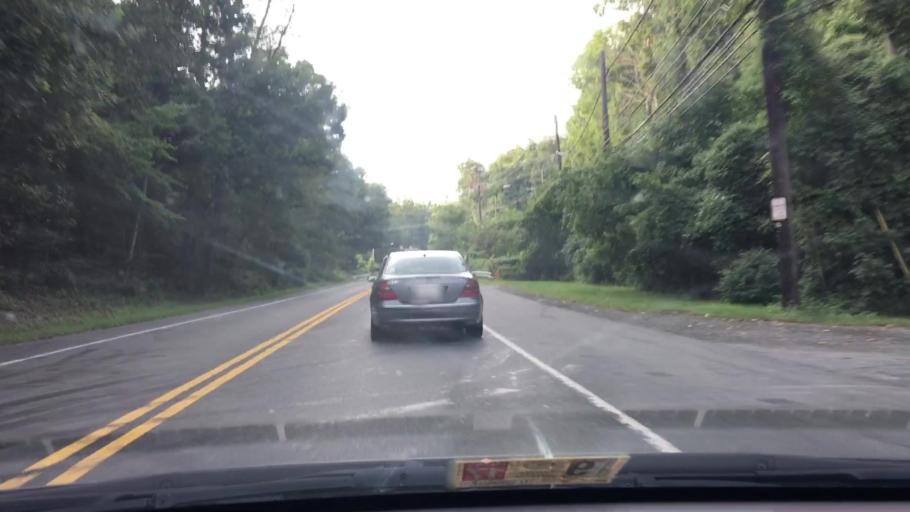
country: US
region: Maryland
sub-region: Montgomery County
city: North Bethesda
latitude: 39.0382
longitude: -77.1590
